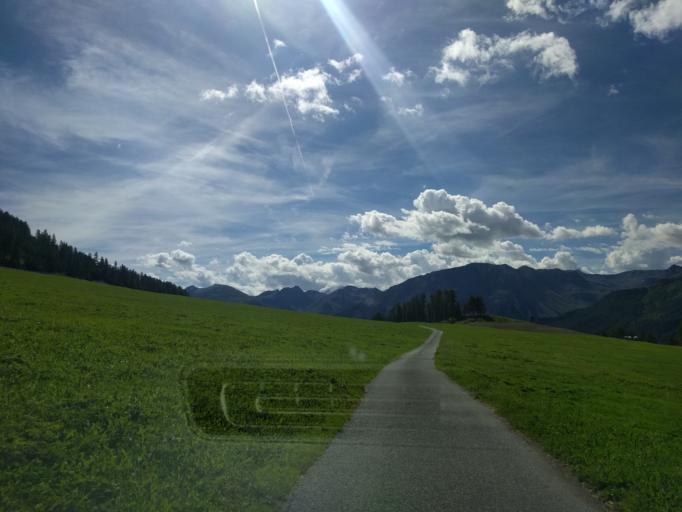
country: IT
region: Trentino-Alto Adige
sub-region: Bolzano
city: Tubre
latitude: 46.6253
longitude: 10.3621
